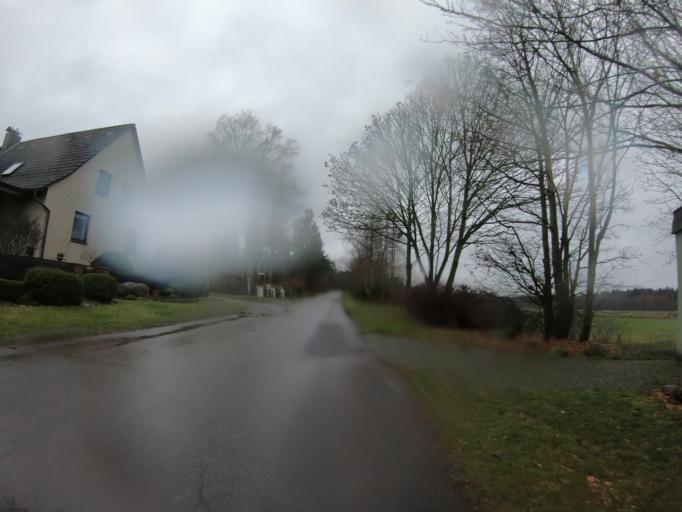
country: DE
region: Lower Saxony
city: Wagenhoff
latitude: 52.4880
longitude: 10.4752
